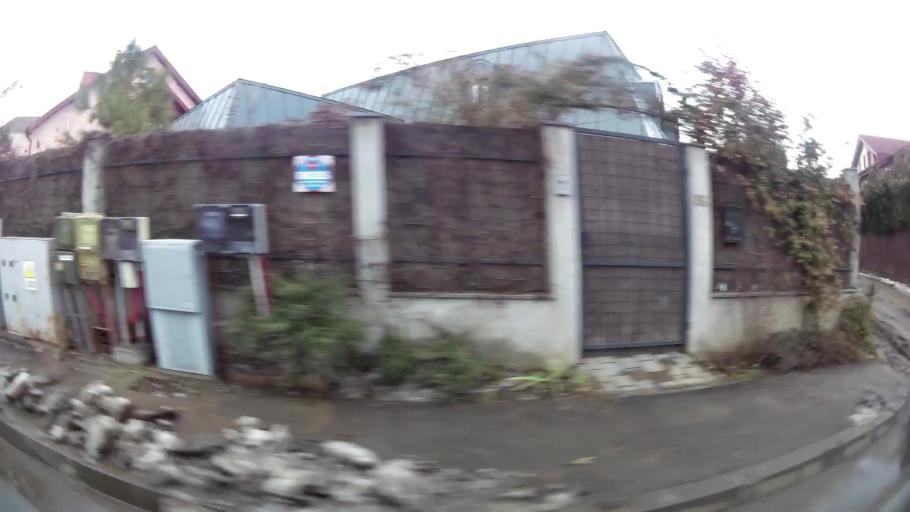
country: RO
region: Ilfov
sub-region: Comuna Otopeni
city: Otopeni
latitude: 44.5051
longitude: 26.0501
